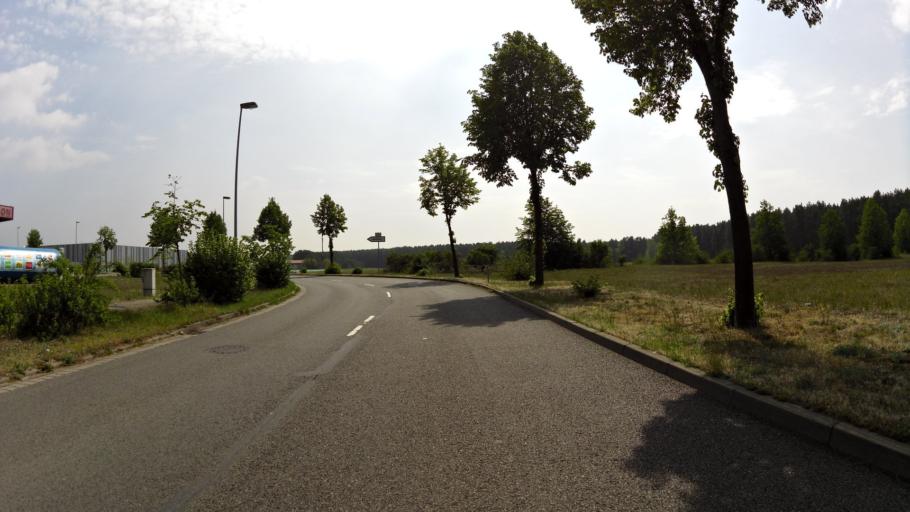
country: DE
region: Brandenburg
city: Grunheide
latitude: 52.3879
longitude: 13.7919
